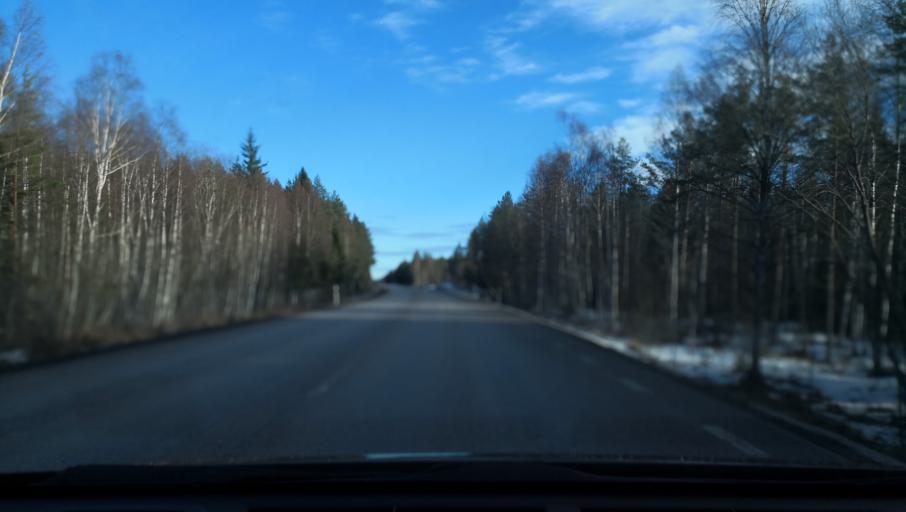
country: SE
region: Uppsala
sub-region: Osthammars Kommun
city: Osterbybruk
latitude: 60.1717
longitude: 17.9312
